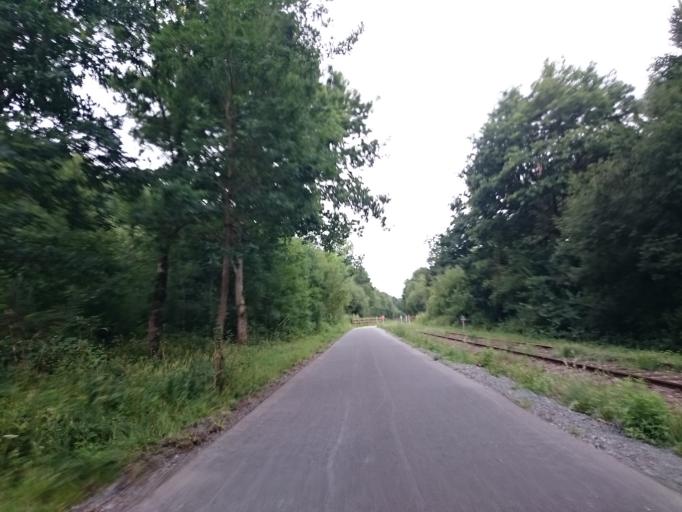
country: FR
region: Lower Normandy
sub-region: Departement du Calvados
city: Clinchamps-sur-Orne
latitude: 49.0838
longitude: -0.4243
